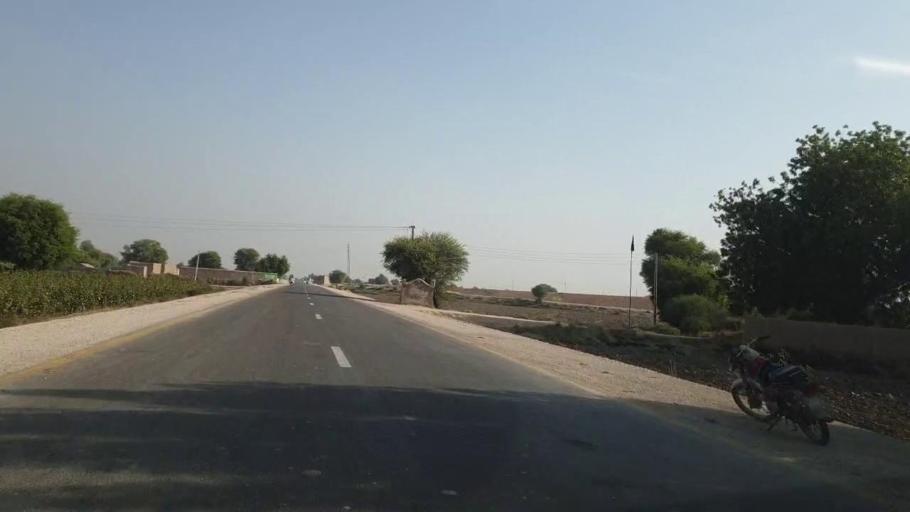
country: PK
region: Sindh
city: Sehwan
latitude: 26.4571
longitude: 67.8063
